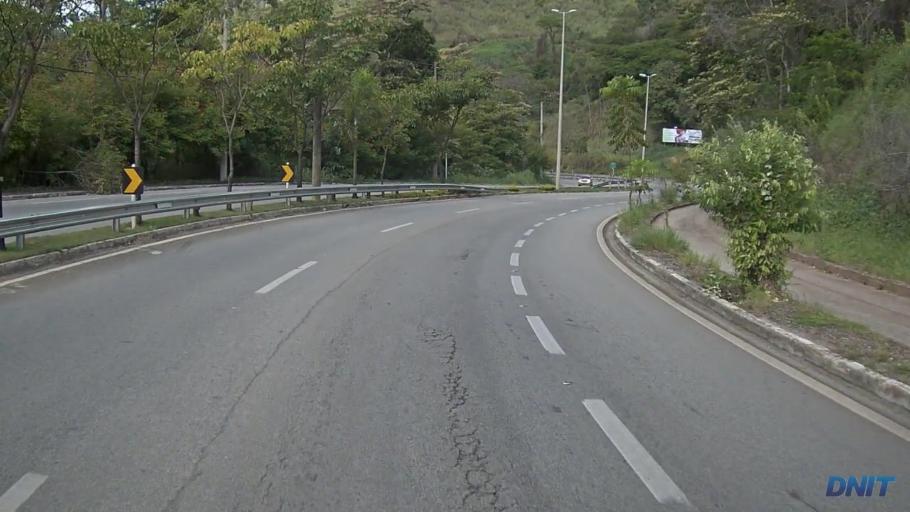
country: BR
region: Minas Gerais
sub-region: Coronel Fabriciano
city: Coronel Fabriciano
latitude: -19.5050
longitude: -42.5888
